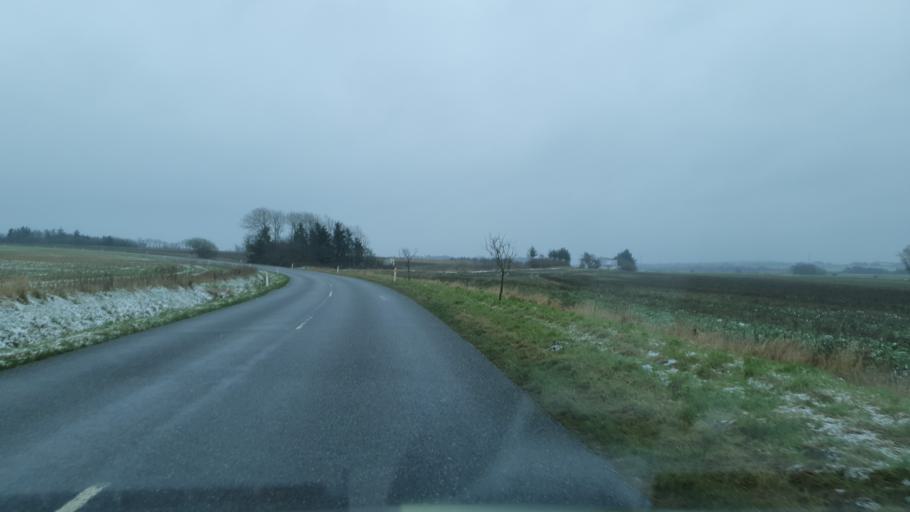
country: DK
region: North Denmark
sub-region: Jammerbugt Kommune
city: Brovst
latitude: 57.1290
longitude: 9.4726
